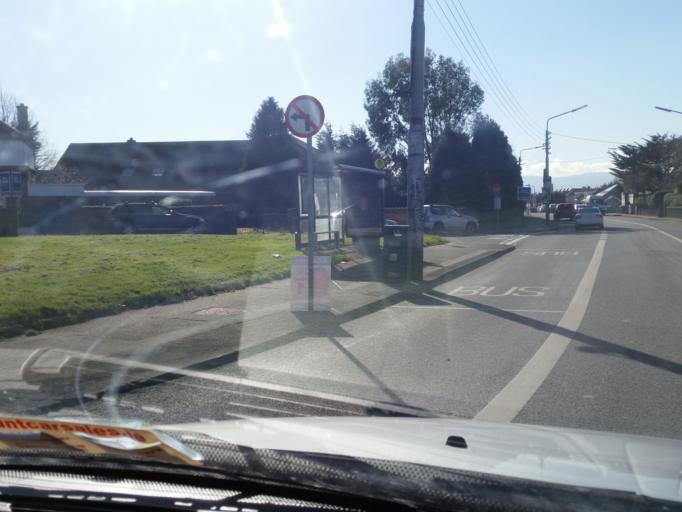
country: IE
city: Killester
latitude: 53.3727
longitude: -6.2020
